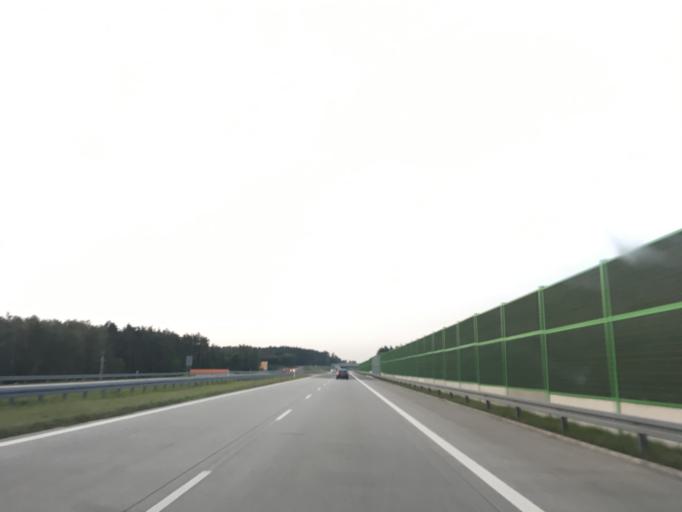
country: PL
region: Lodz Voivodeship
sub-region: Powiat lodzki wschodni
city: Tuszyn
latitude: 51.5686
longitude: 19.5994
